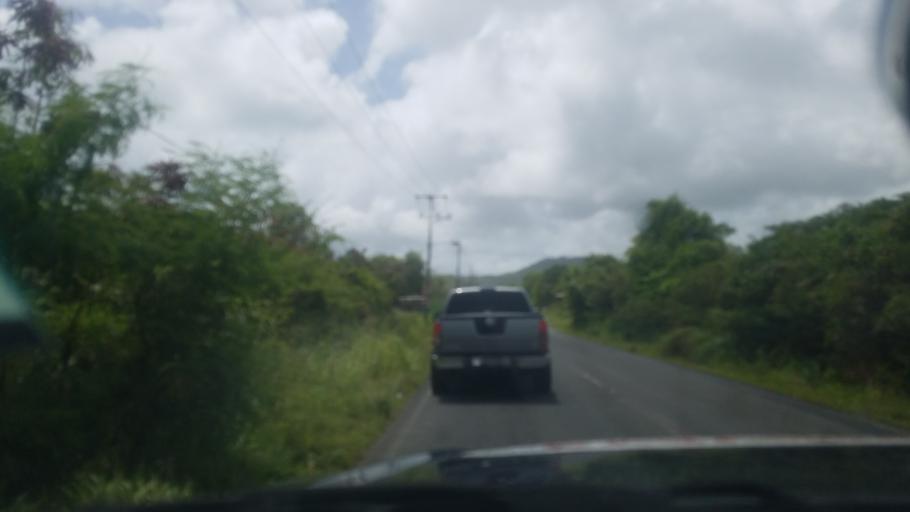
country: LC
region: Laborie Quarter
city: Laborie
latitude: 13.7403
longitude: -60.9756
